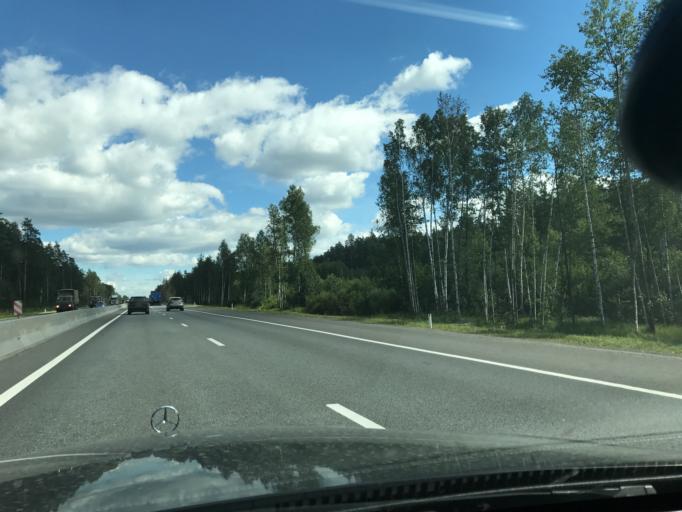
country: RU
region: Nizjnij Novgorod
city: Yuganets
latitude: 56.2888
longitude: 43.2482
